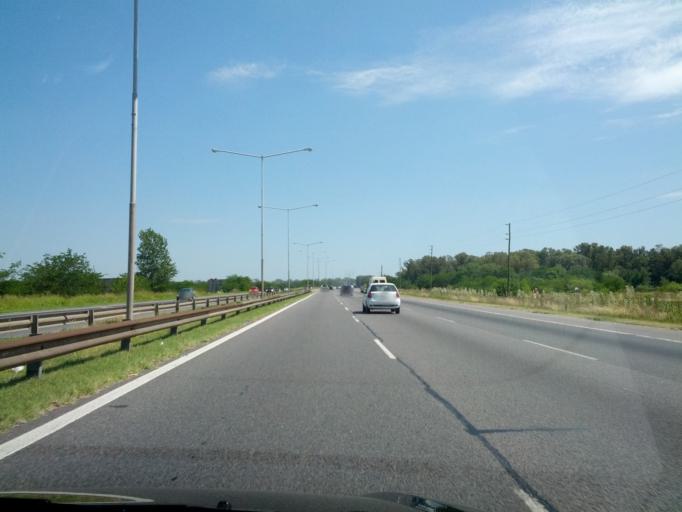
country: AR
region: Buenos Aires
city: Belen de Escobar
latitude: -34.3012
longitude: -58.8801
